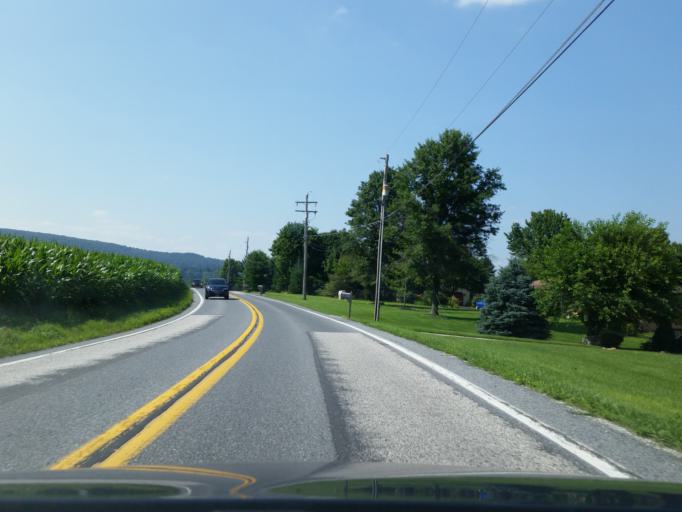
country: US
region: Pennsylvania
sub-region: York County
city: Hallam
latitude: 39.9884
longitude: -76.6101
